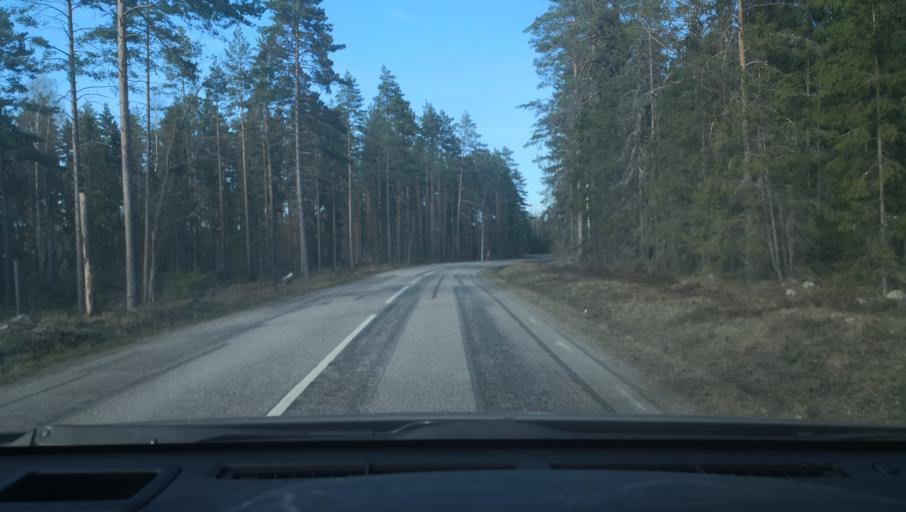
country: SE
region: Uppsala
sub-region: Heby Kommun
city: Morgongava
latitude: 60.0032
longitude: 16.9319
